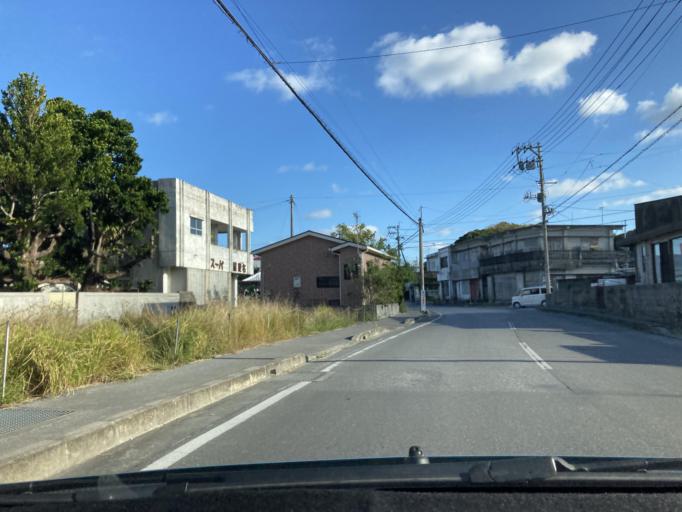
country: JP
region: Okinawa
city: Katsuren-haebaru
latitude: 26.3242
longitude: 127.9062
